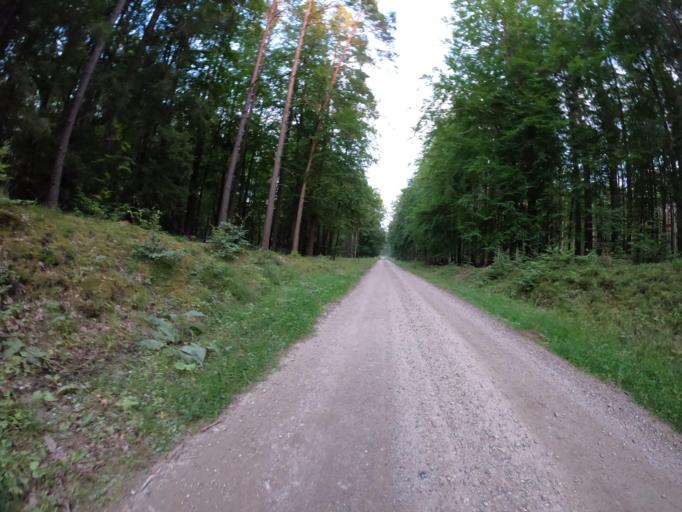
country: PL
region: West Pomeranian Voivodeship
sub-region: Powiat koszalinski
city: Sianow
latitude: 54.1015
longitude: 16.3761
